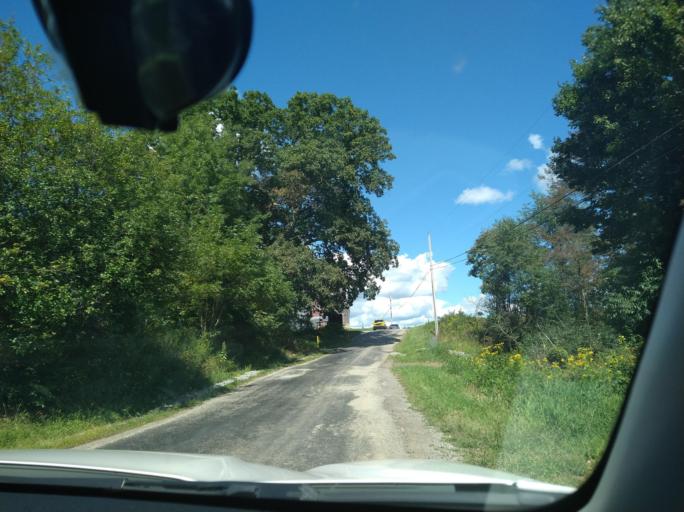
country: US
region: Pennsylvania
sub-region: Fayette County
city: Bear Rocks
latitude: 40.0952
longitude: -79.3650
